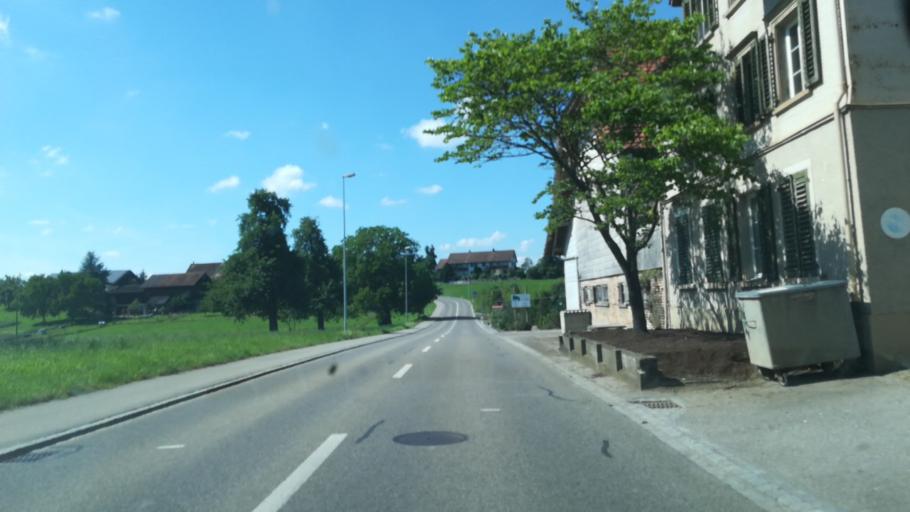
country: CH
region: Thurgau
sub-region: Weinfelden District
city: Sulgen
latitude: 47.5468
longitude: 9.1804
